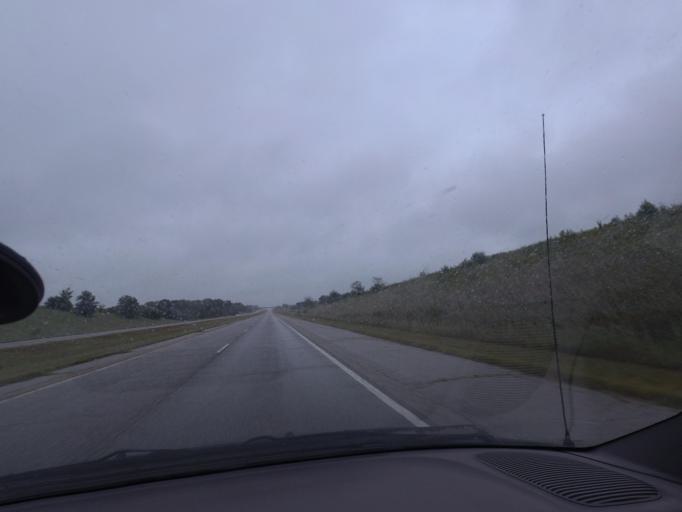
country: US
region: Illinois
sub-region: Pike County
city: Barry
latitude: 39.6905
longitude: -90.9263
